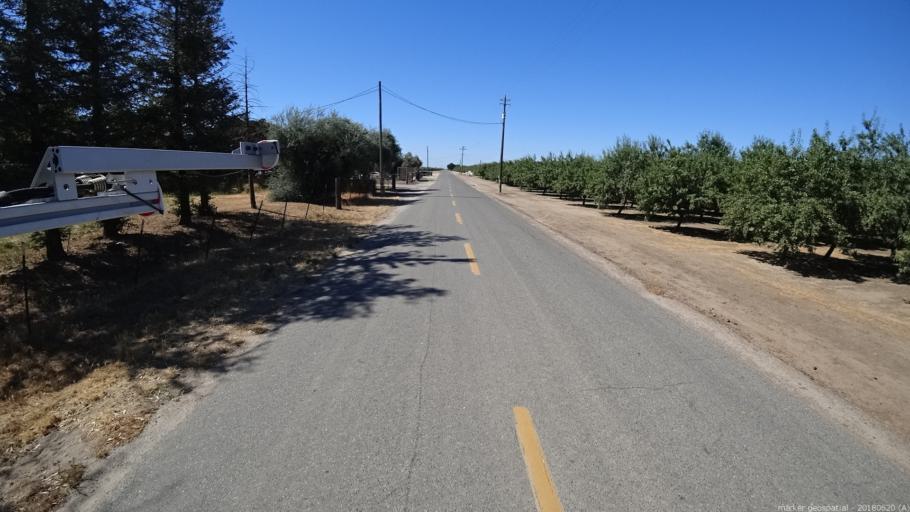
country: US
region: California
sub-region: Madera County
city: Parkwood
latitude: 36.8888
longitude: -120.0285
